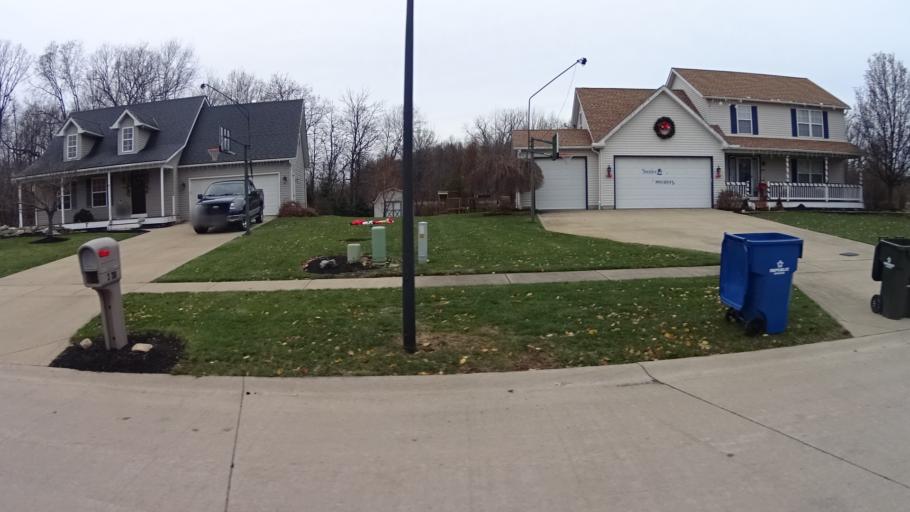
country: US
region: Ohio
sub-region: Lorain County
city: North Ridgeville
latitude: 41.3640
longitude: -82.0068
